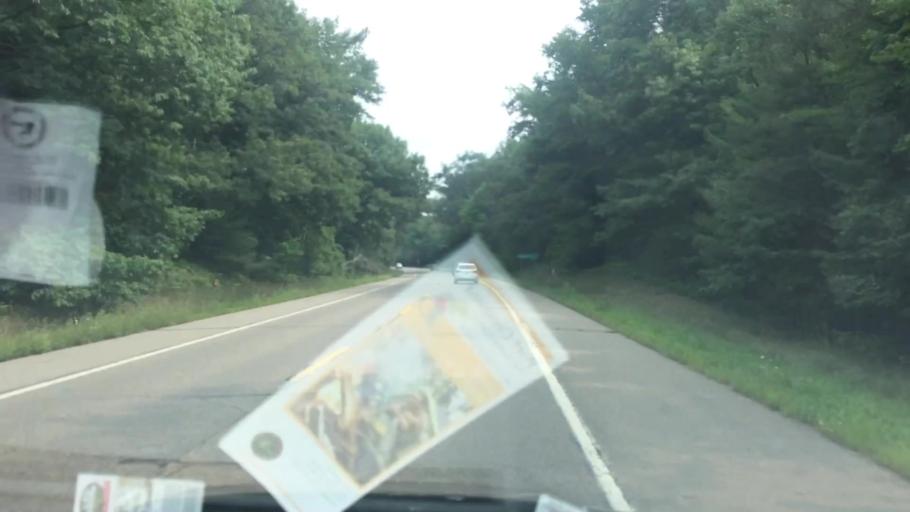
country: US
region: Michigan
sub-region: Huron County
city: Bad Axe
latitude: 43.9969
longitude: -83.0606
